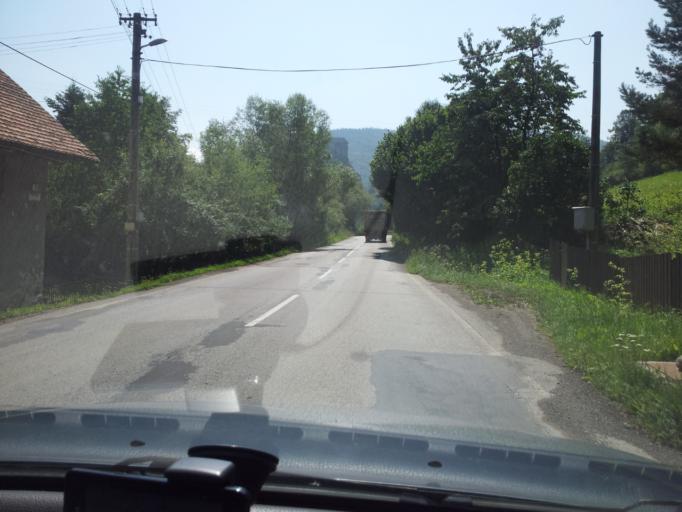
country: SK
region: Zilinsky
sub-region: Okres Dolny Kubin
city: Dolny Kubin
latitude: 49.2666
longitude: 19.3544
